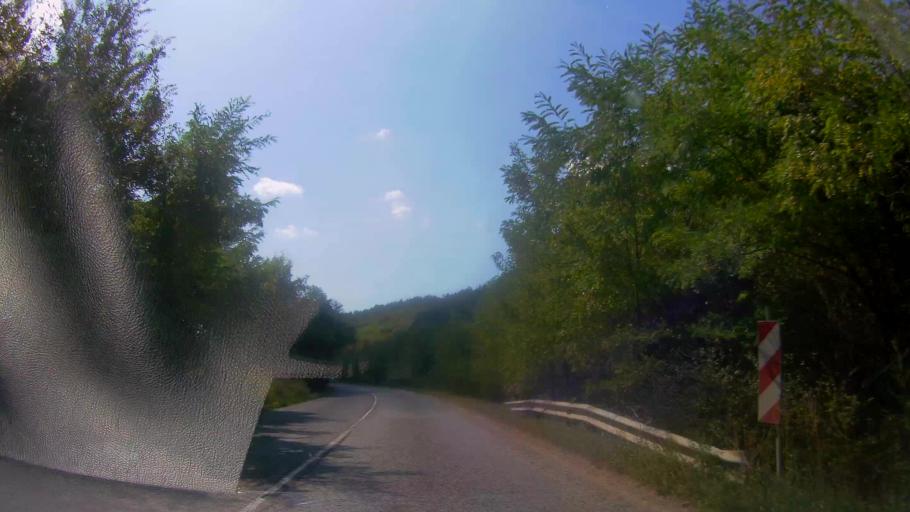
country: BG
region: Veliko Turnovo
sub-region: Obshtina Polski Trumbesh
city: Polski Trumbesh
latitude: 43.4399
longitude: 25.6543
